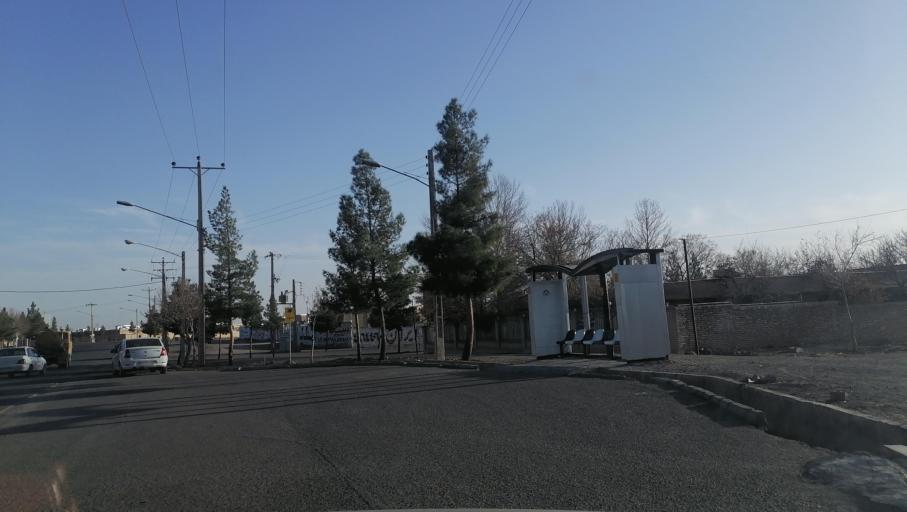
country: IR
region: Razavi Khorasan
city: Sabzevar
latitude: 36.2780
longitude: 57.6758
